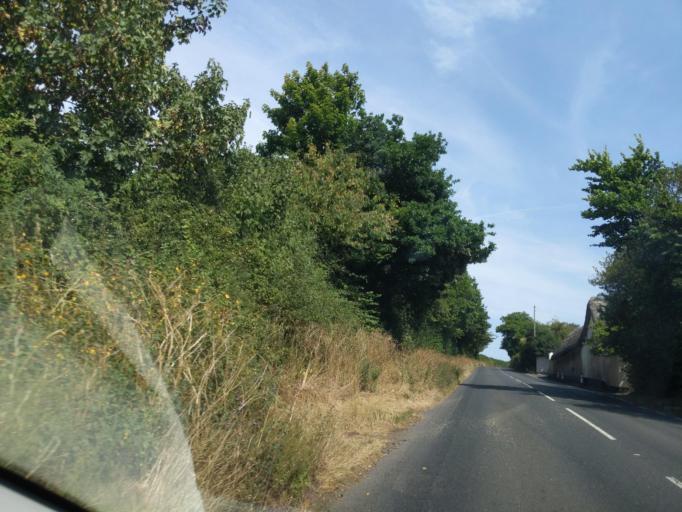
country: GB
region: England
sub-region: Devon
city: Okehampton
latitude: 50.7988
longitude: -3.9926
